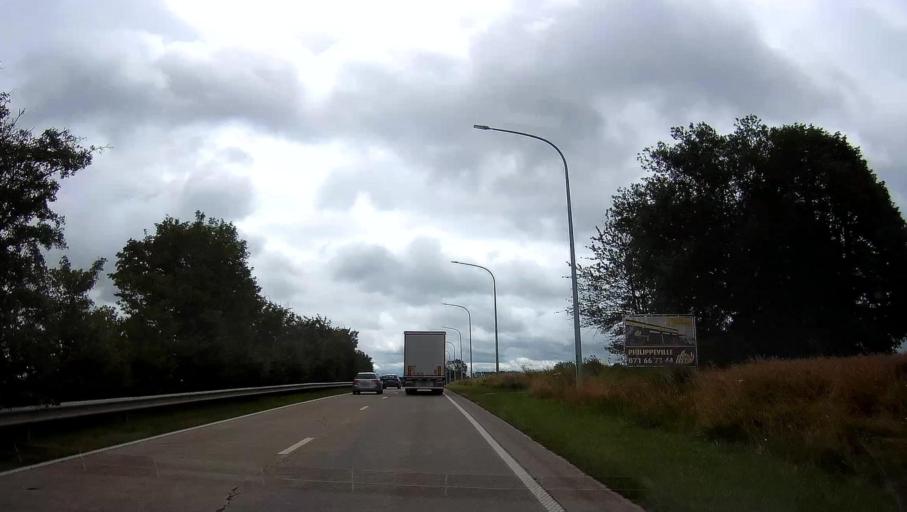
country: BE
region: Wallonia
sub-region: Province de Namur
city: Philippeville
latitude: 50.2109
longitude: 4.5204
